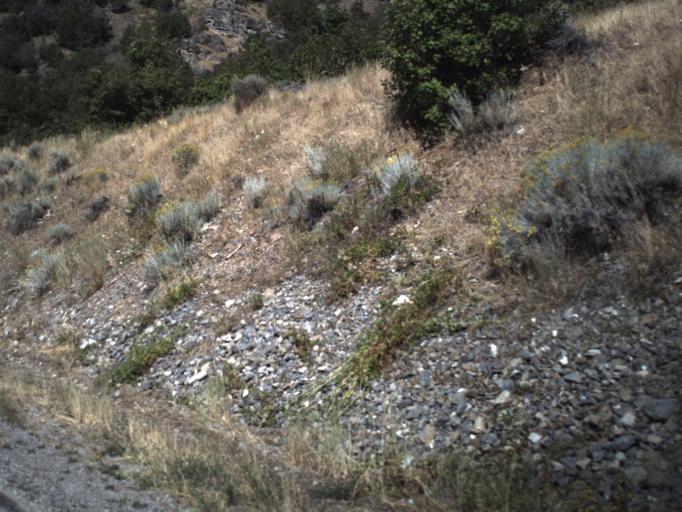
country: US
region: Utah
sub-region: Cache County
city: Millville
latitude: 41.6217
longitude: -111.7564
